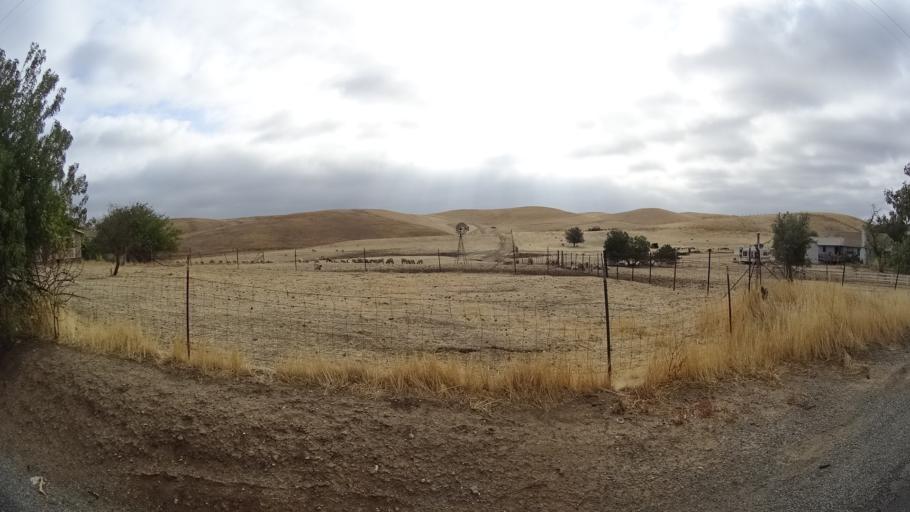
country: US
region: California
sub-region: Yolo County
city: Dunnigan
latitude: 38.7895
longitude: -121.9168
